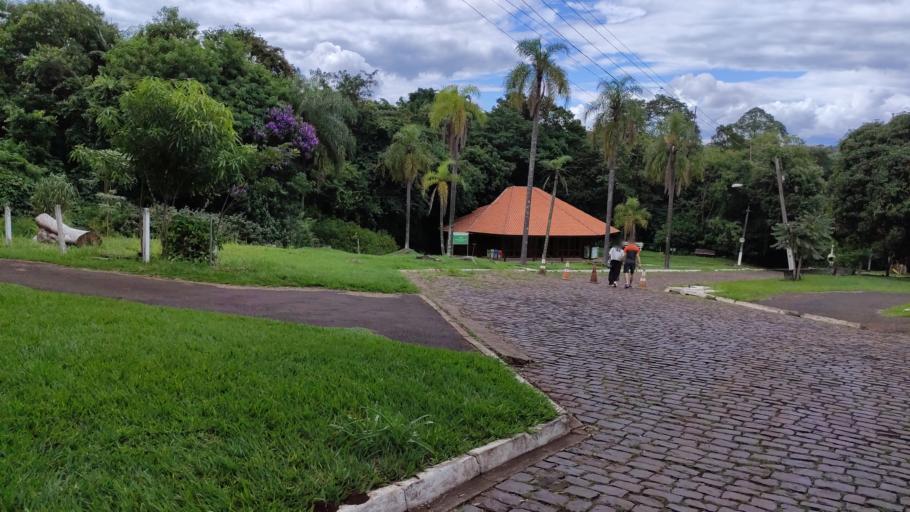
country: BR
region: Parana
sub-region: Londrina
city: Londrina
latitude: -23.3460
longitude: -51.1421
